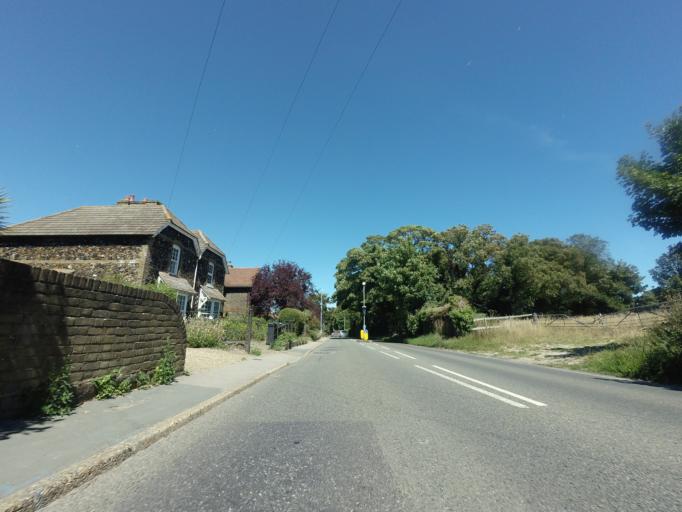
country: GB
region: England
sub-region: Kent
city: Deal
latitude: 51.1972
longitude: 1.3856
